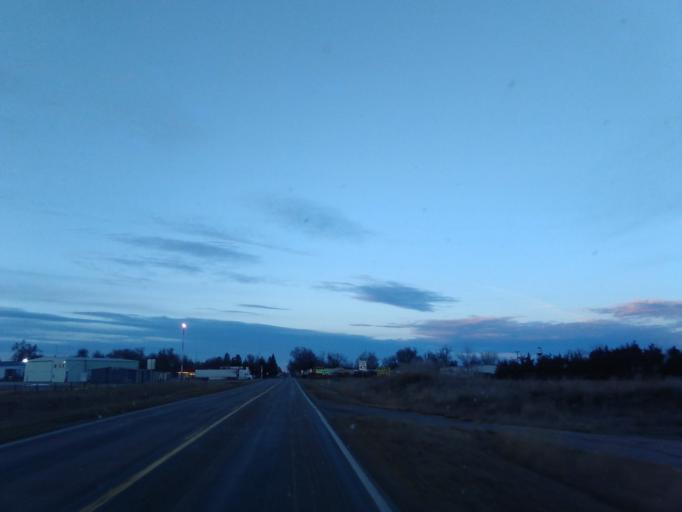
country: US
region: Nebraska
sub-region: Garden County
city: Oshkosh
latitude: 41.3996
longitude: -102.3475
